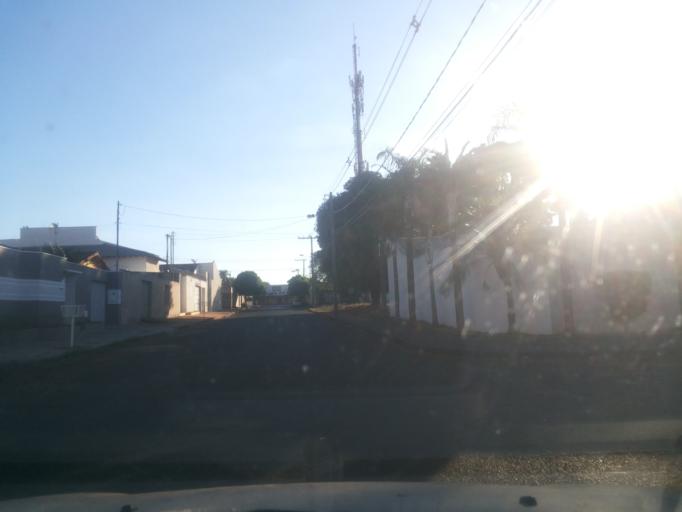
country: BR
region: Minas Gerais
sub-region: Ituiutaba
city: Ituiutaba
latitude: -18.9927
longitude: -49.4539
